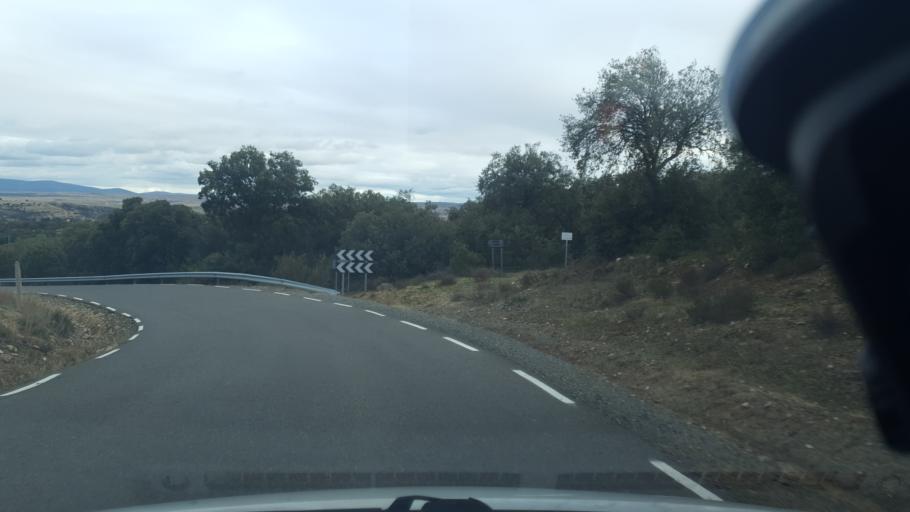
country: ES
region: Castille and Leon
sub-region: Provincia de Avila
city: Gotarrendura
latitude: 40.8252
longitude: -4.7096
